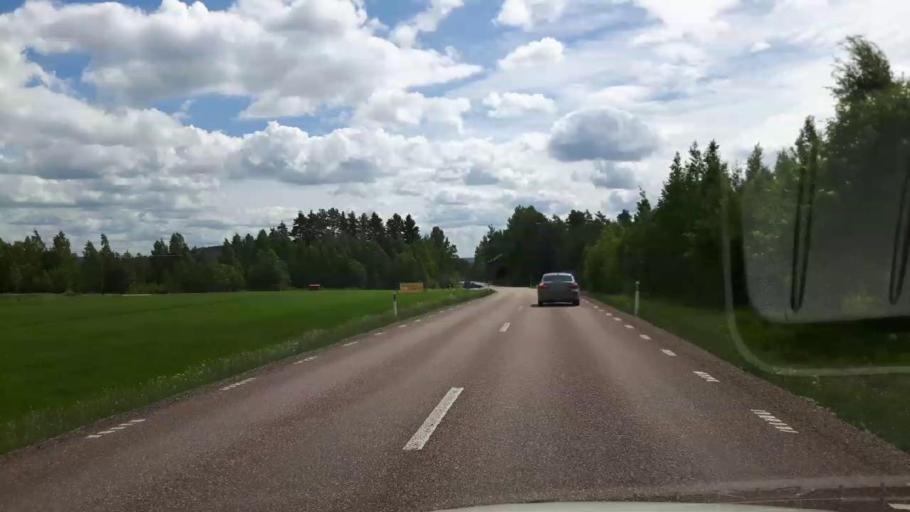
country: SE
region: Dalarna
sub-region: Saters Kommun
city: Saeter
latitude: 60.4239
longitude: 15.8408
